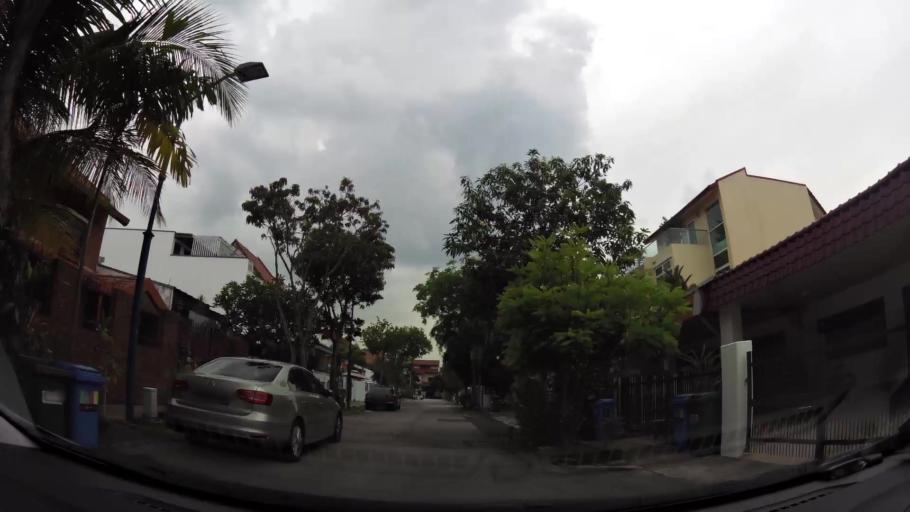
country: SG
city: Singapore
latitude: 1.3672
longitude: 103.8679
